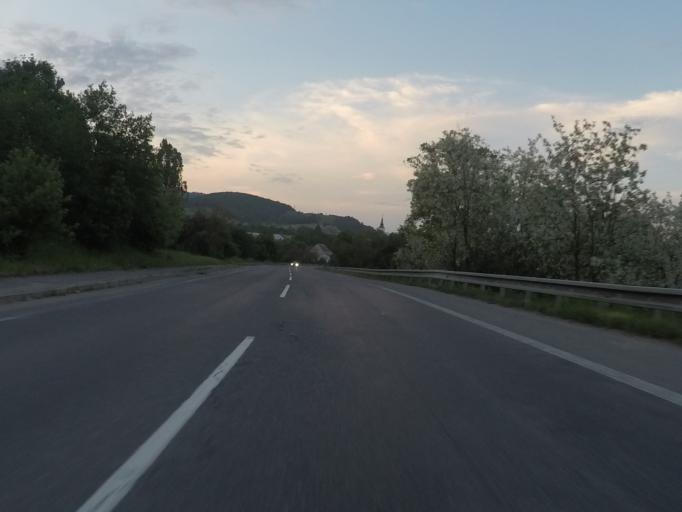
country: SK
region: Banskobystricky
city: Rimavska Sobota
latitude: 48.5048
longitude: 19.9378
